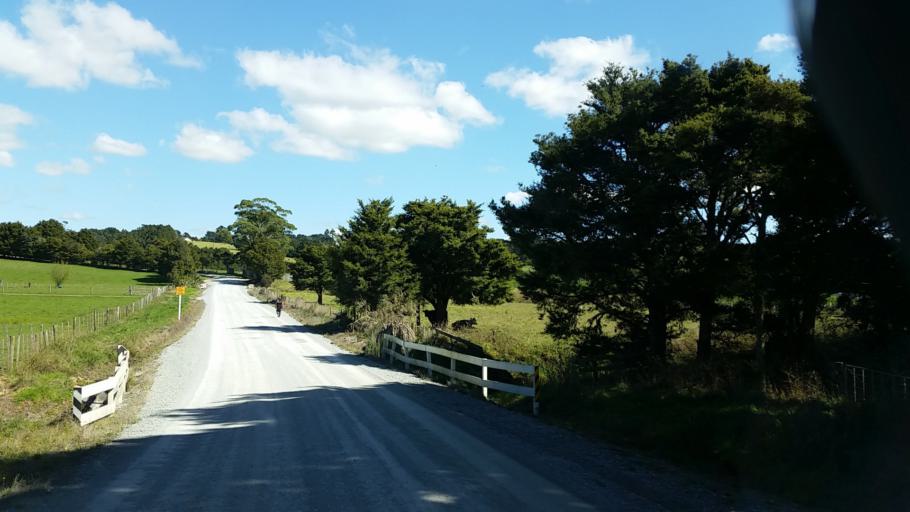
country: NZ
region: Northland
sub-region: Whangarei
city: Maungatapere
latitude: -35.6948
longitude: 174.2154
